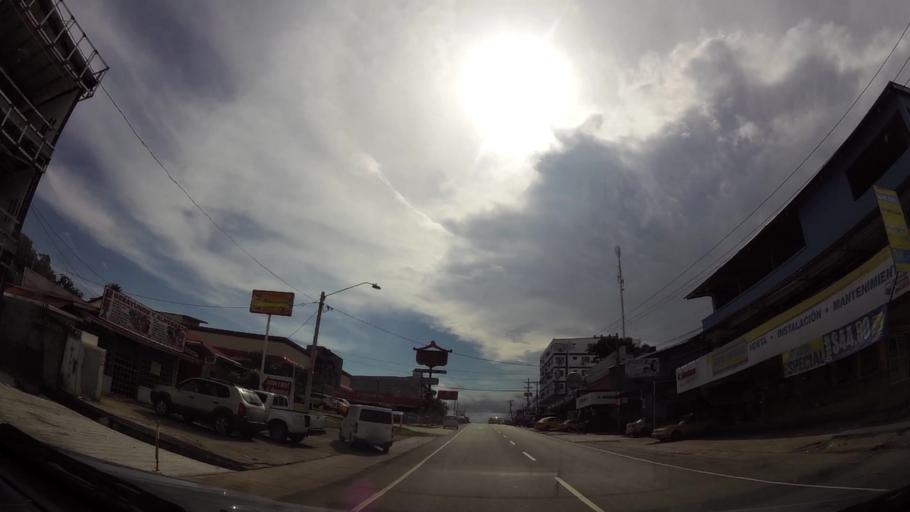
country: PA
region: Panama
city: La Chorrera
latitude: 8.8837
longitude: -79.7770
